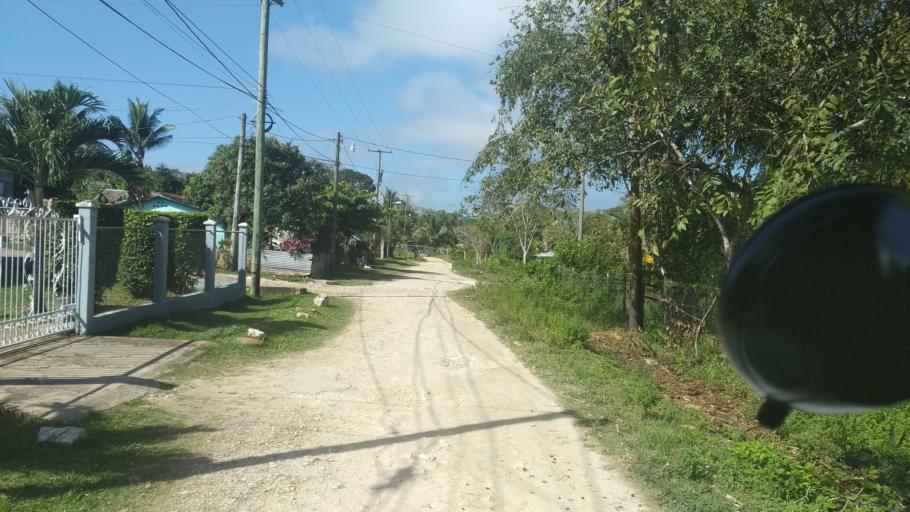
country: BZ
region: Cayo
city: Benque Viejo del Carmen
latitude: 17.0851
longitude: -89.1323
